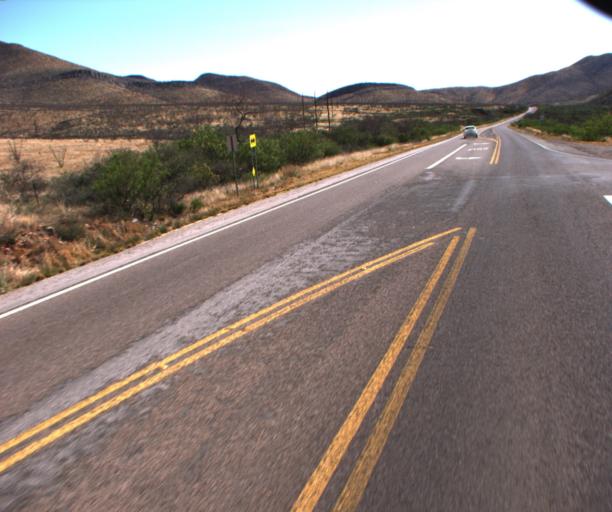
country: US
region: Arizona
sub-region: Cochise County
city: Bisbee
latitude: 31.4302
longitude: -109.8651
